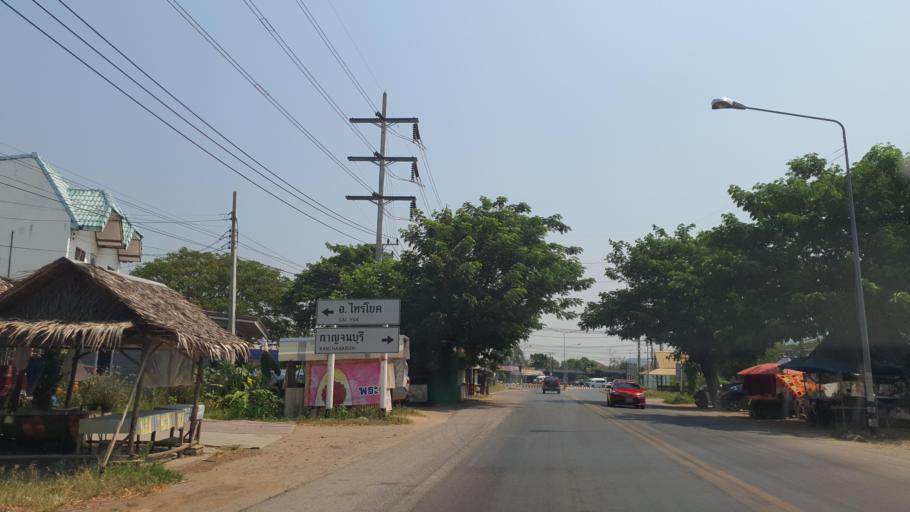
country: TH
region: Kanchanaburi
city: Kanchanaburi
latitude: 14.0587
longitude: 99.4771
